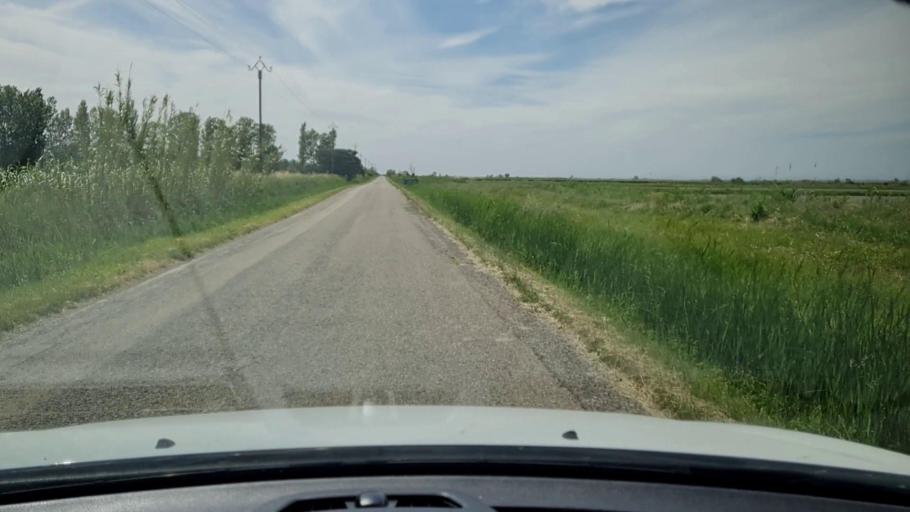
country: FR
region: Languedoc-Roussillon
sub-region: Departement du Gard
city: Saint-Gilles
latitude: 43.5895
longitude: 4.4415
